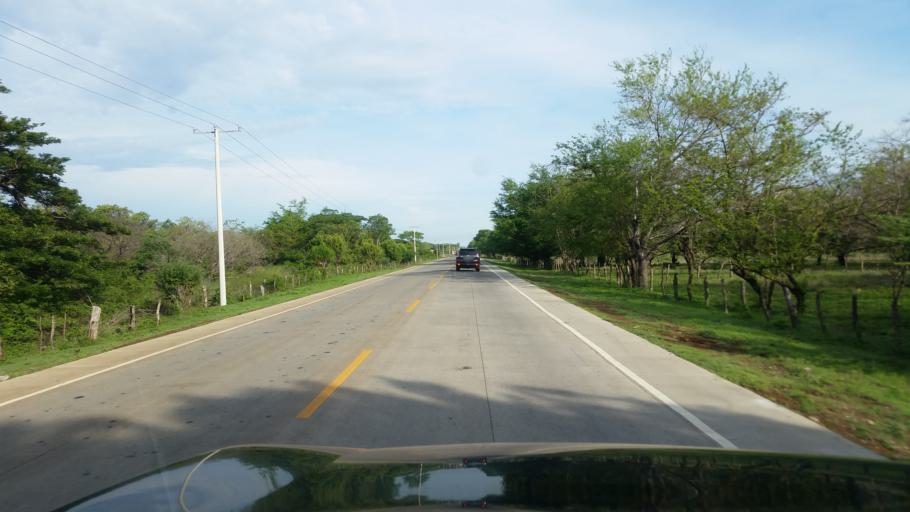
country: NI
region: Managua
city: Carlos Fonseca Amador
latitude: 12.0945
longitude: -86.5542
